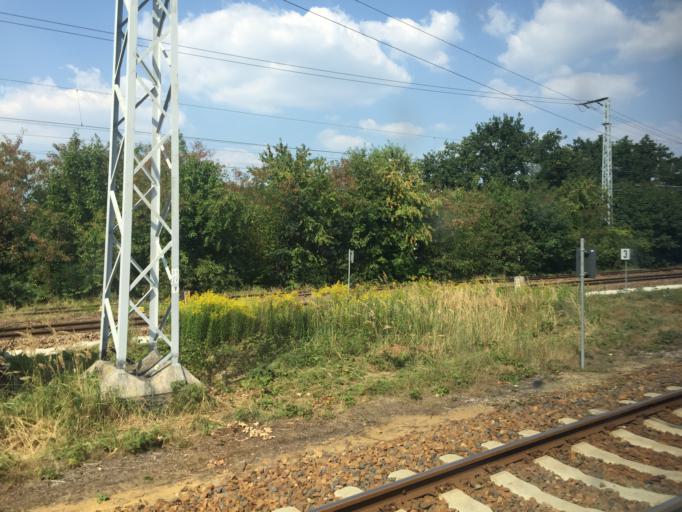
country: DE
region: Brandenburg
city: Ruhland
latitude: 51.4572
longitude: 13.8728
